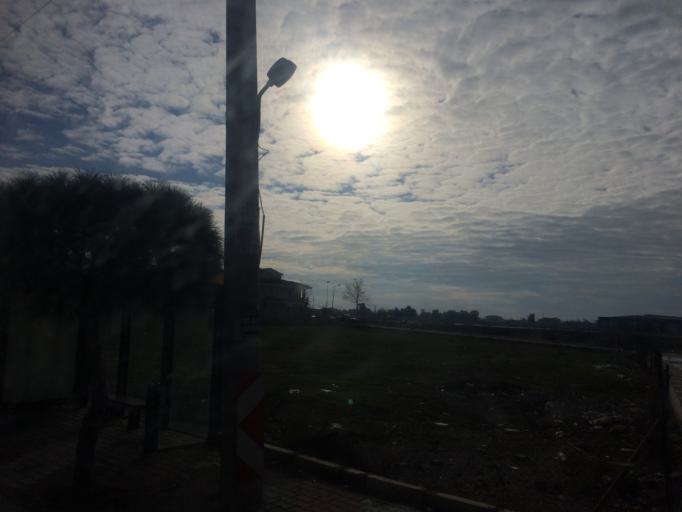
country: TR
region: Izmir
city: Menemen
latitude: 38.5035
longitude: 26.9592
